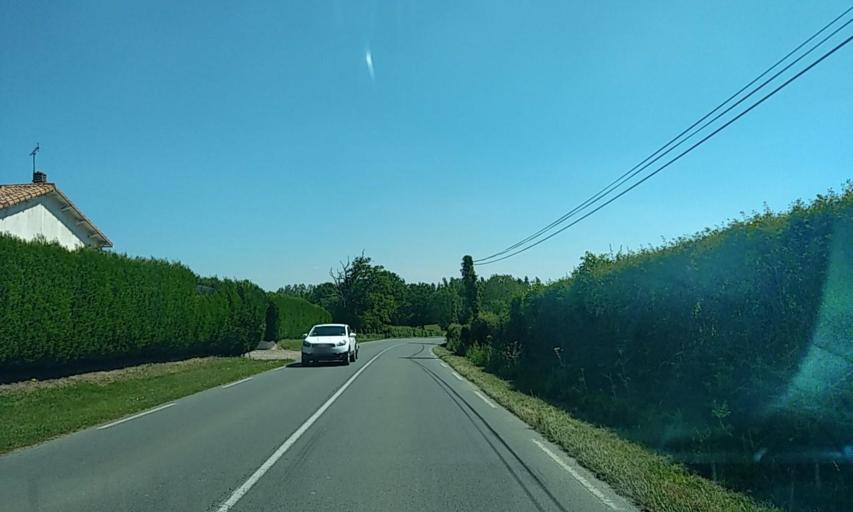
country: FR
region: Poitou-Charentes
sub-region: Departement des Deux-Sevres
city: La Chapelle-Saint-Laurent
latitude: 46.7871
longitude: -0.4791
